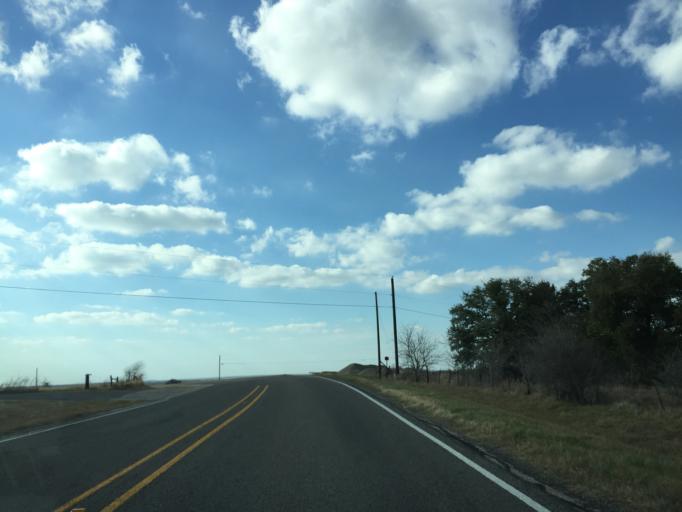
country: US
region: Texas
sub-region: Williamson County
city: Taylor
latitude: 30.6387
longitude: -97.4203
